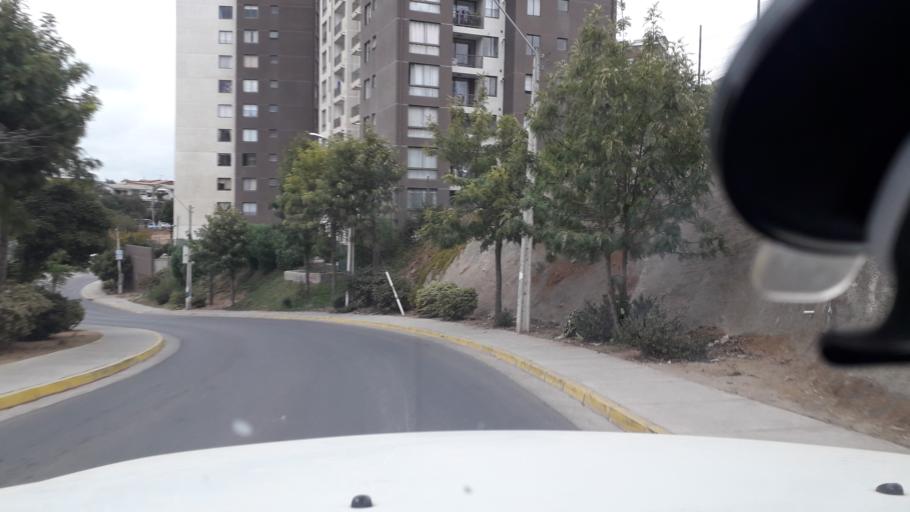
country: CL
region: Valparaiso
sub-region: Provincia de Marga Marga
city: Quilpue
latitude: -33.0340
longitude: -71.4817
